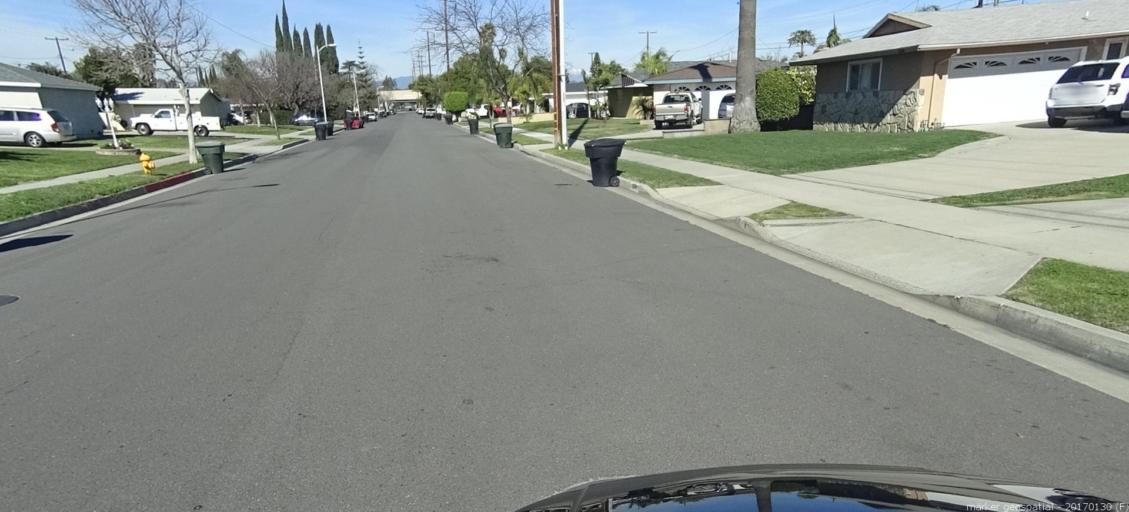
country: US
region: California
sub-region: Orange County
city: Buena Park
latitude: 33.8509
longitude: -117.9679
